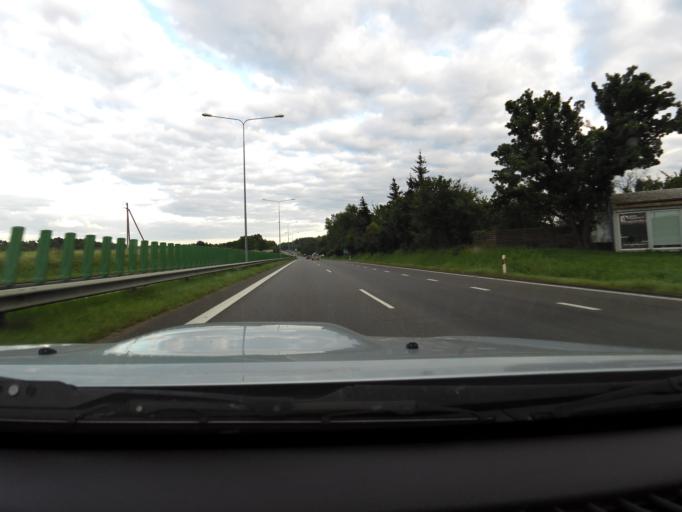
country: LT
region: Kauno apskritis
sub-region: Kauno rajonas
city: Karmelava
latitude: 54.9153
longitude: 24.0945
